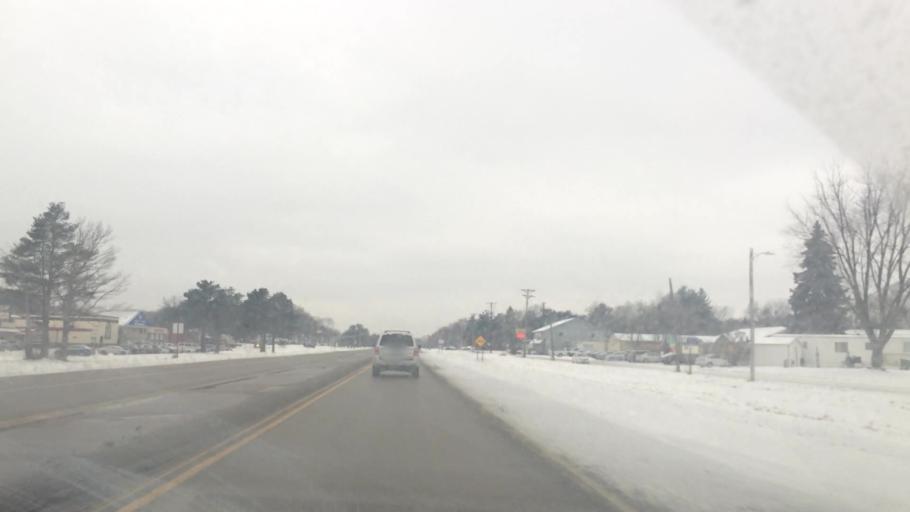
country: US
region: Minnesota
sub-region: Anoka County
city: Lexington
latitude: 45.1374
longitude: -93.1701
